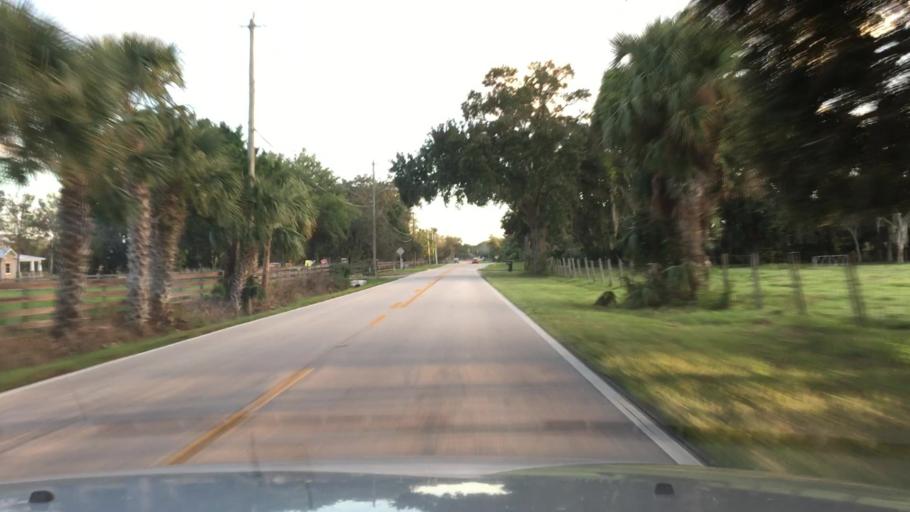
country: US
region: Florida
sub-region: Volusia County
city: Ormond Beach
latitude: 29.2822
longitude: -81.1130
